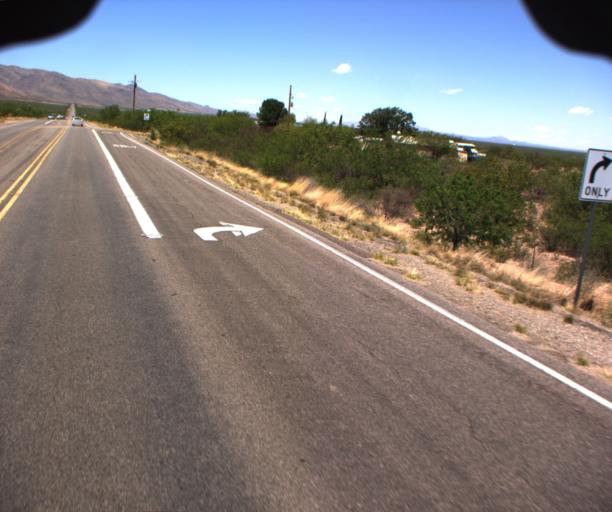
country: US
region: Arizona
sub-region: Cochise County
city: Bisbee
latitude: 31.4004
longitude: -109.7754
